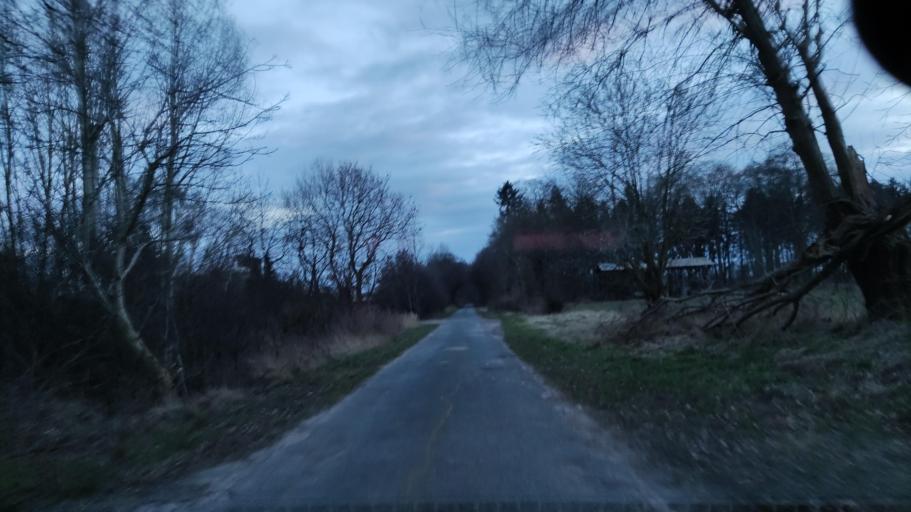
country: DE
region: Lower Saxony
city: Natendorf
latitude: 53.0696
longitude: 10.4297
